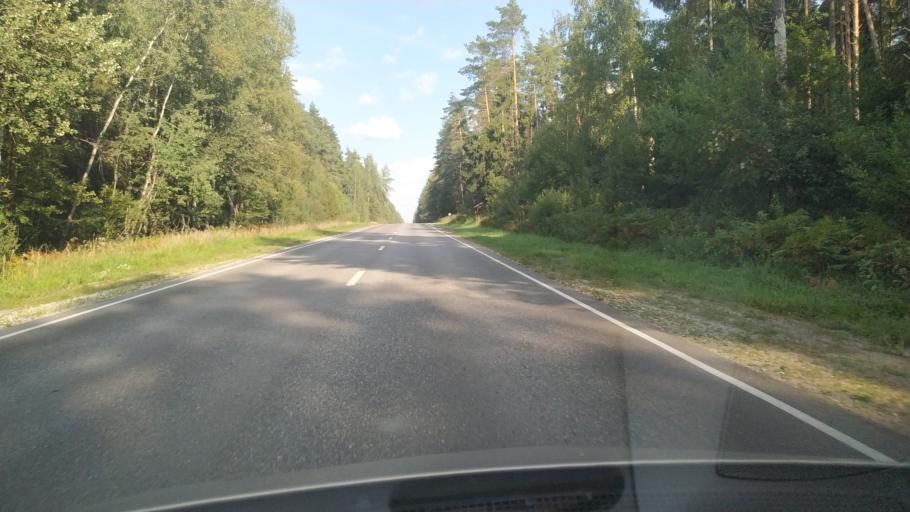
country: RU
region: Moskovskaya
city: Vereya
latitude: 55.7024
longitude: 39.2007
